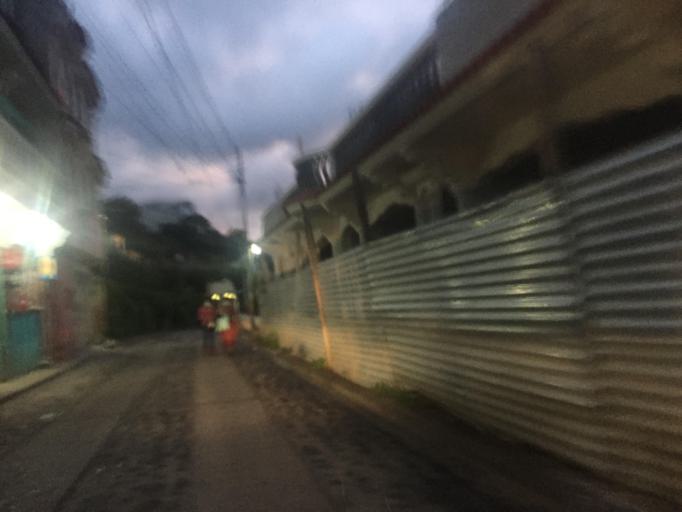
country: GT
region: Totonicapan
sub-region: Municipio de Totonicapan
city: Totonicapan
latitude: 14.9177
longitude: -91.3550
